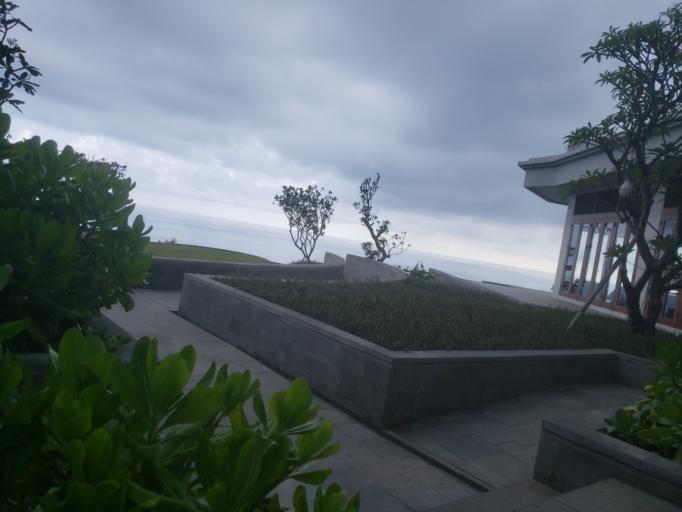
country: ID
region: Bali
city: Kangin
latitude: -8.8462
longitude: 115.1299
